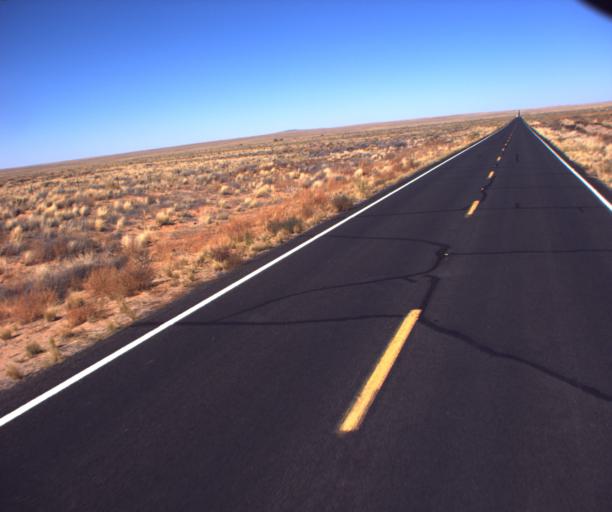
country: US
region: Arizona
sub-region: Navajo County
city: Dilkon
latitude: 35.5673
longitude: -110.4589
